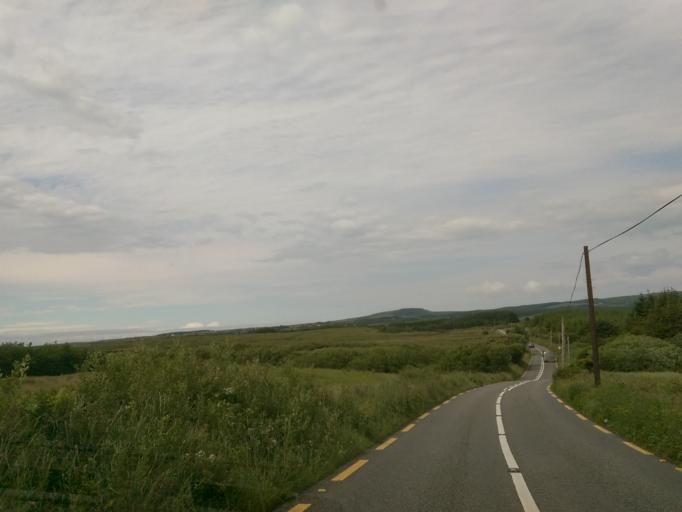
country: IE
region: Connaught
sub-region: County Galway
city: Bearna
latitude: 53.0045
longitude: -9.3145
